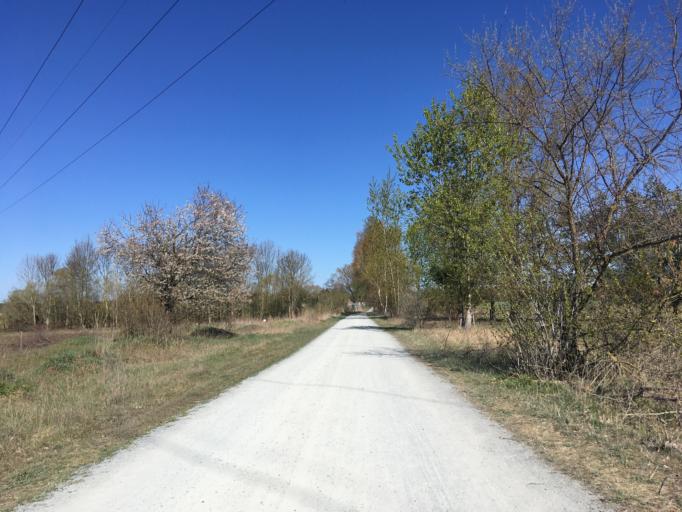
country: DE
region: Berlin
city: Buch
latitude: 52.6736
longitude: 13.4813
